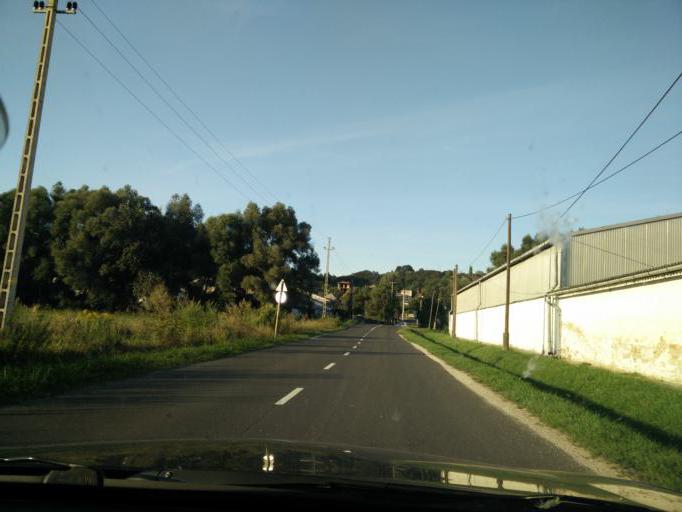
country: HU
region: Komarom-Esztergom
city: Piliscsev
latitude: 47.6533
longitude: 18.7882
